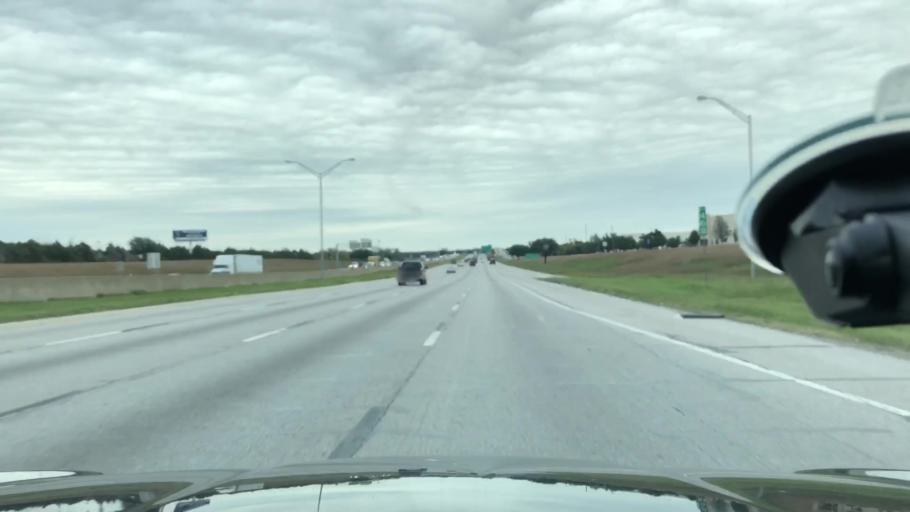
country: US
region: Texas
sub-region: Dallas County
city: DeSoto
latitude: 32.6420
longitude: -96.8183
